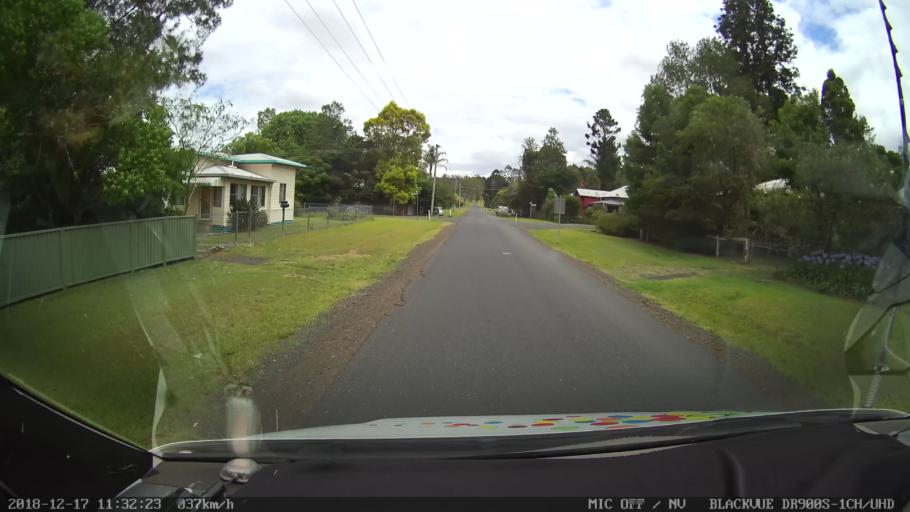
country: AU
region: New South Wales
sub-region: Kyogle
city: Kyogle
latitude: -28.7358
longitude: 152.6199
